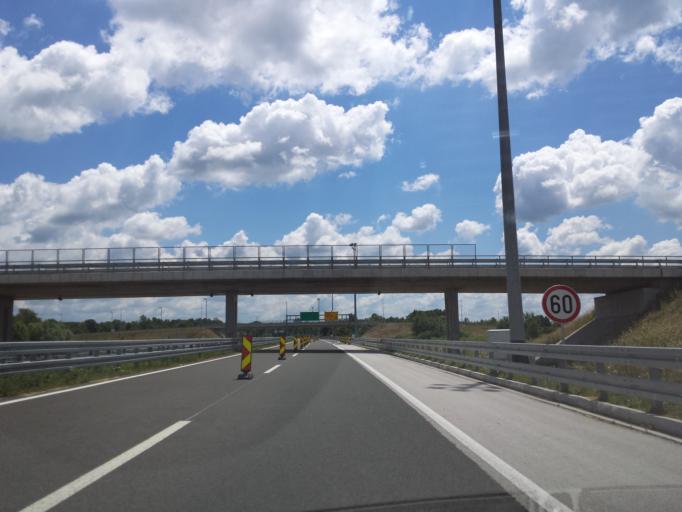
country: HR
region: Sisacko-Moslavacka
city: Lekenik
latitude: 45.5655
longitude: 16.2147
